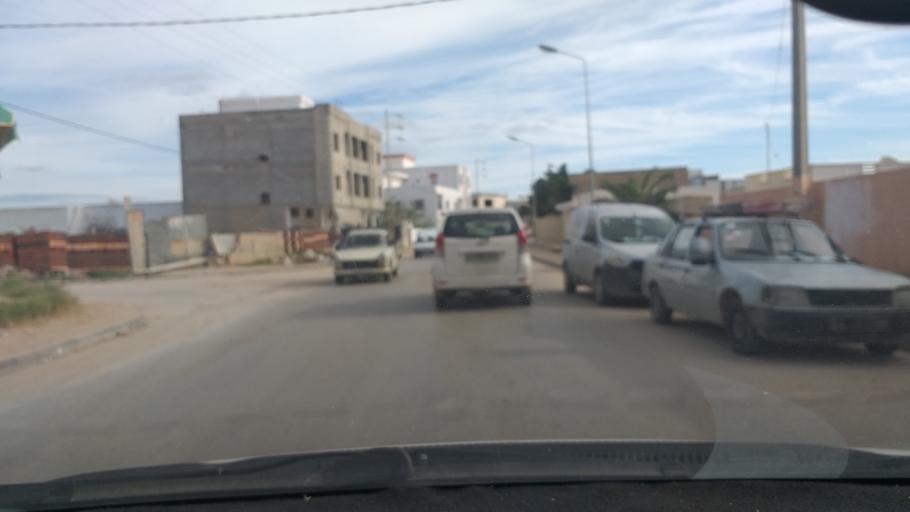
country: TN
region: Safaqis
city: Al Qarmadah
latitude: 34.7936
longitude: 10.8032
